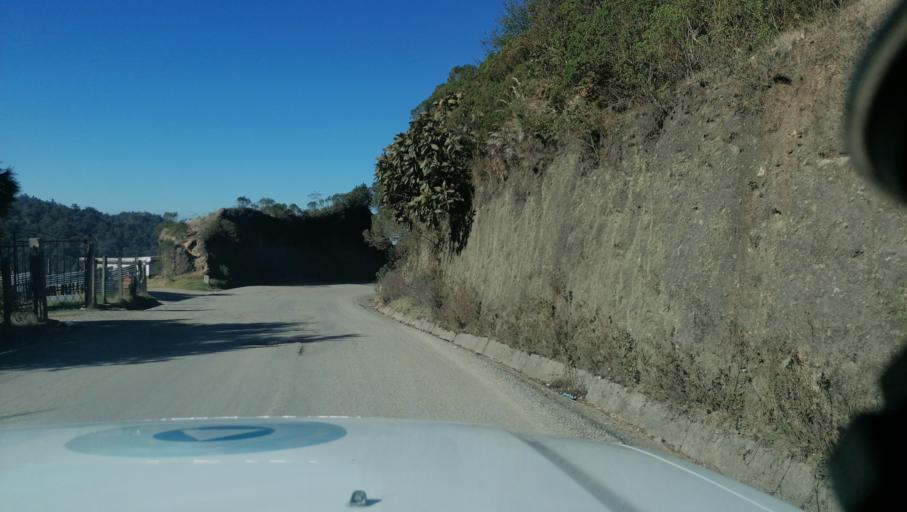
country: MX
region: Chiapas
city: Motozintla de Mendoza
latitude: 15.2661
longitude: -92.2217
